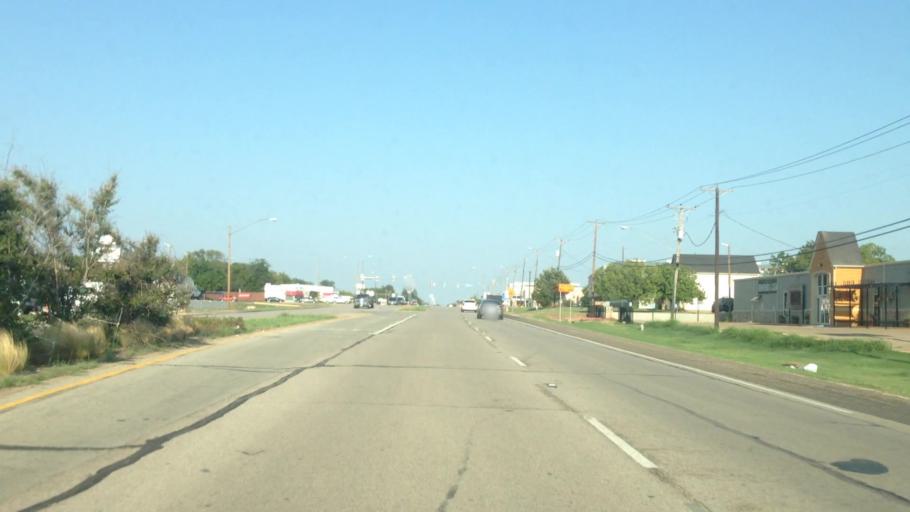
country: US
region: Texas
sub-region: Tarrant County
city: Richland Hills
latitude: 32.8092
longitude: -97.2410
